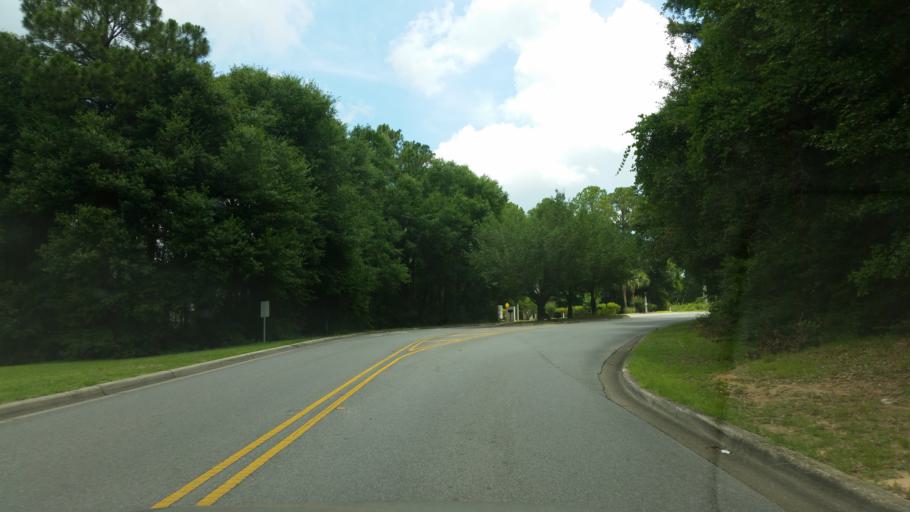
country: US
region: Florida
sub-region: Escambia County
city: Brent
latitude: 30.4793
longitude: -87.2675
